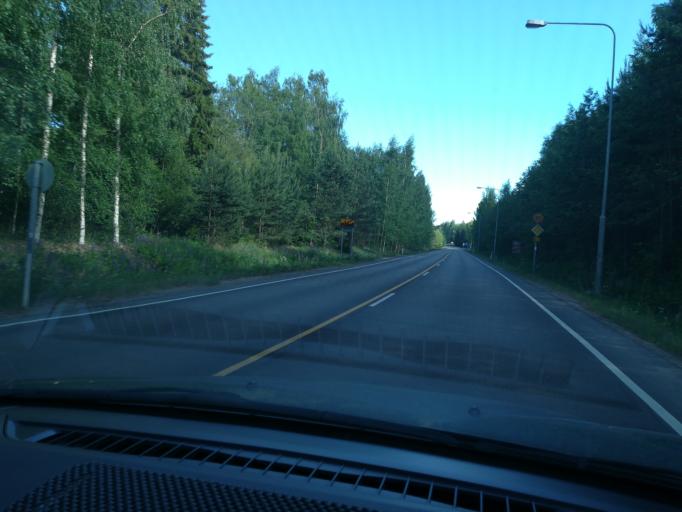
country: FI
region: Southern Savonia
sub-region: Mikkeli
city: Puumala
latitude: 61.5149
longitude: 28.1744
